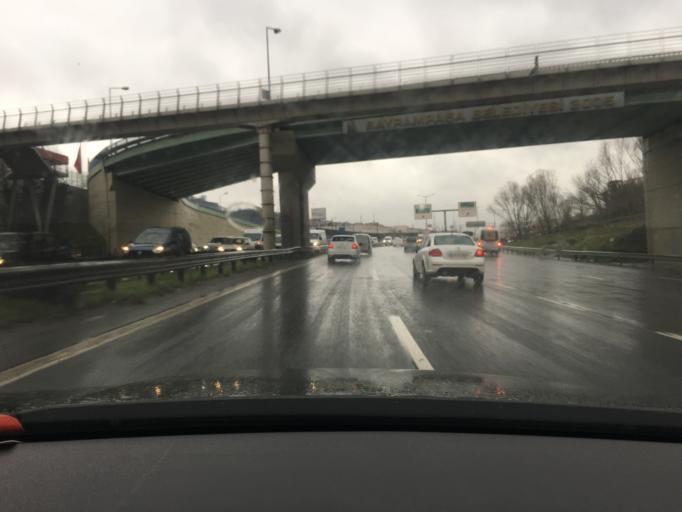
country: TR
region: Istanbul
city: Esenler
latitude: 41.0376
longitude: 28.8893
